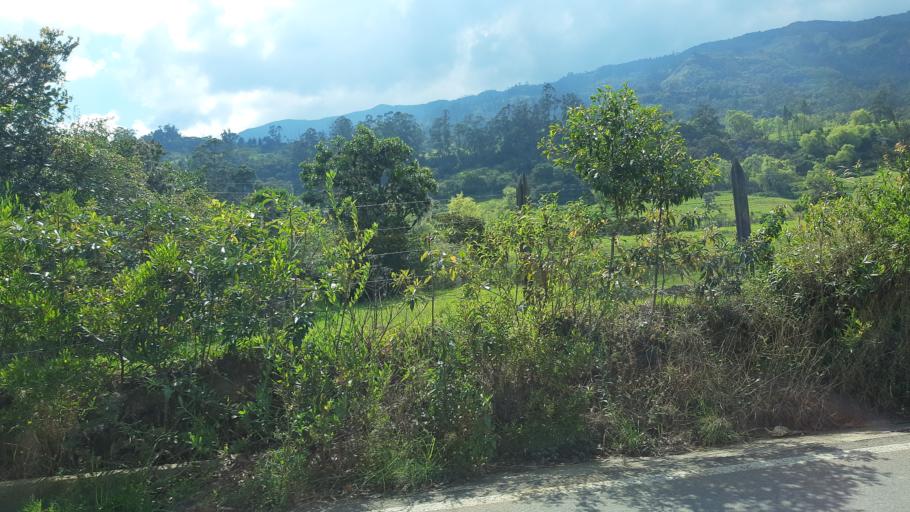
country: CO
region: Boyaca
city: Santa Sofia
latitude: 5.7725
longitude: -73.6027
